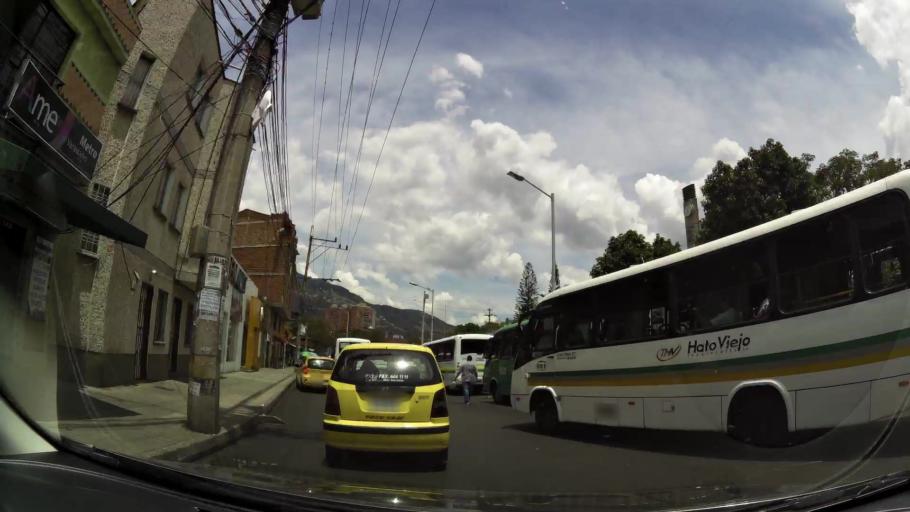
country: CO
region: Antioquia
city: Bello
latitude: 6.3309
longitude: -75.5546
